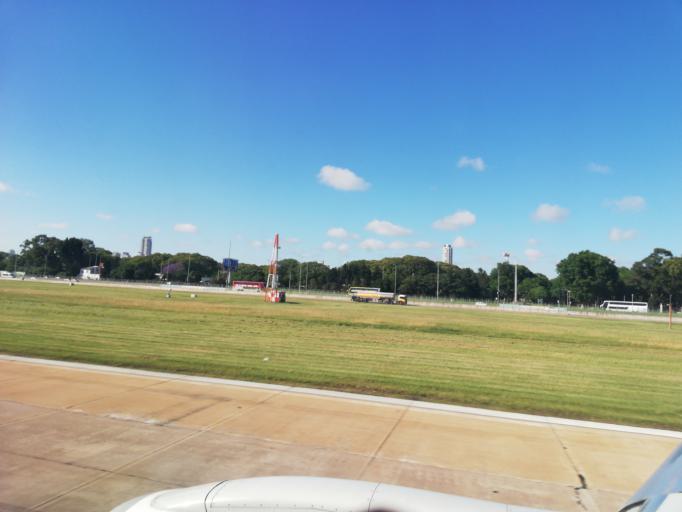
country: AR
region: Buenos Aires F.D.
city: Colegiales
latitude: -34.5552
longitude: -58.4231
